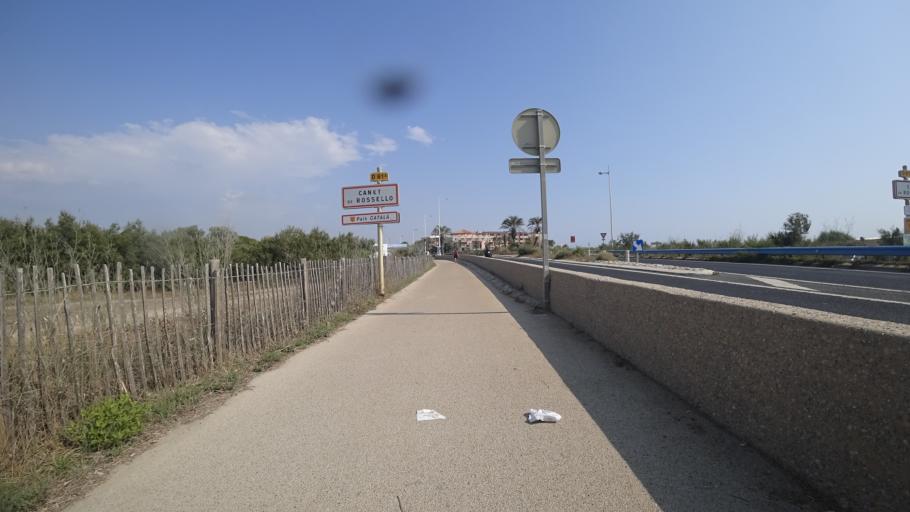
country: FR
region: Languedoc-Roussillon
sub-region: Departement des Pyrenees-Orientales
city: Canet-en-Roussillon
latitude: 42.6725
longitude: 3.0331
